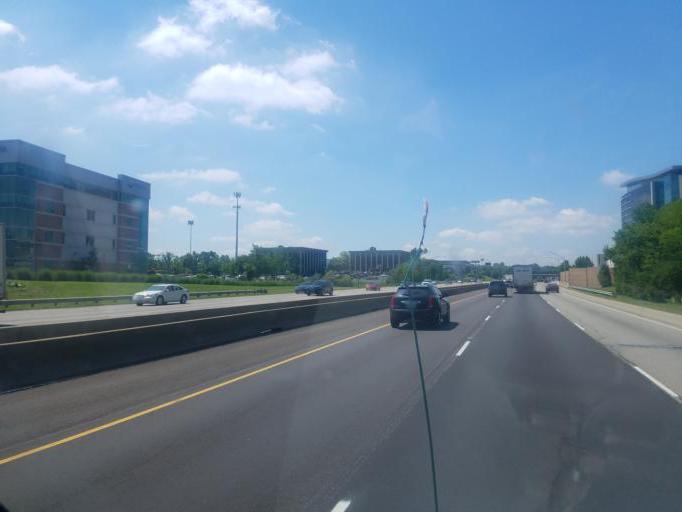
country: US
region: Ohio
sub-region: Hamilton County
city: Kenwood
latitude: 39.2076
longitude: -84.3713
